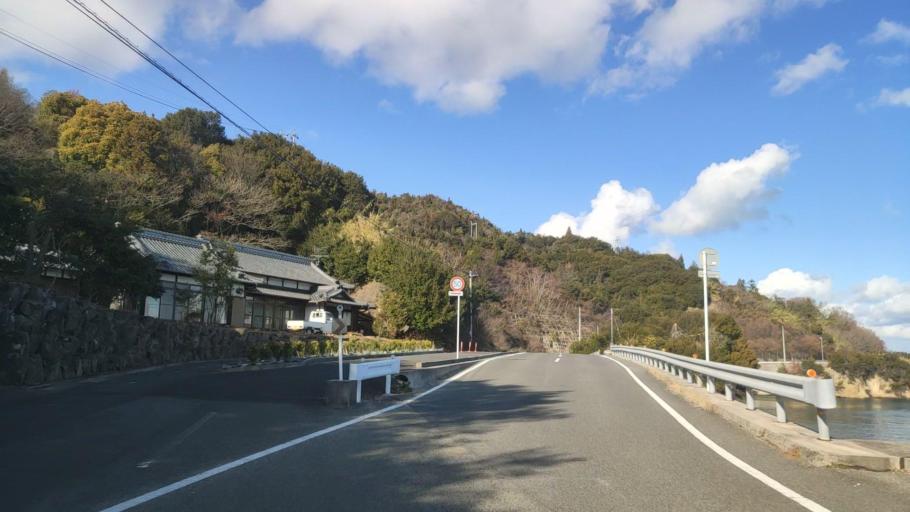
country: JP
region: Hiroshima
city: Innoshima
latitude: 34.2243
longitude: 133.1082
